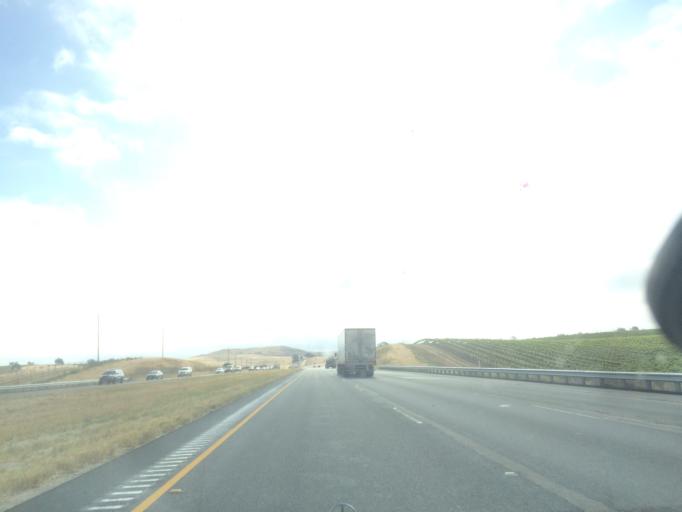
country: US
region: California
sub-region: San Luis Obispo County
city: Paso Robles
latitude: 35.6594
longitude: -120.5565
